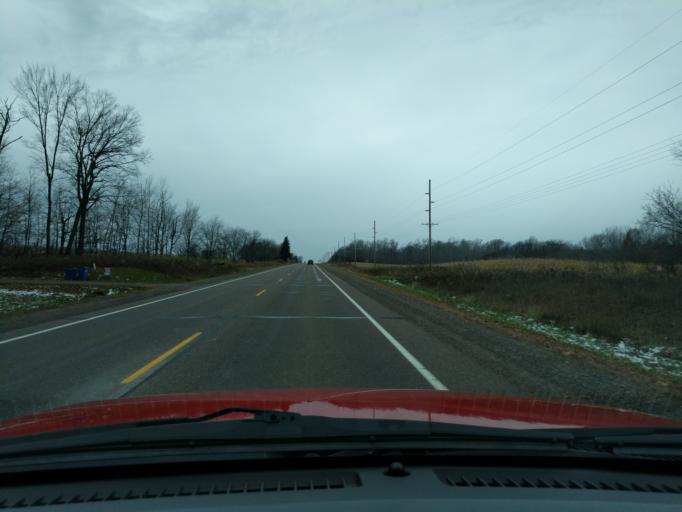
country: US
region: Wisconsin
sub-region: Washburn County
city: Shell Lake
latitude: 45.8153
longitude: -92.0271
